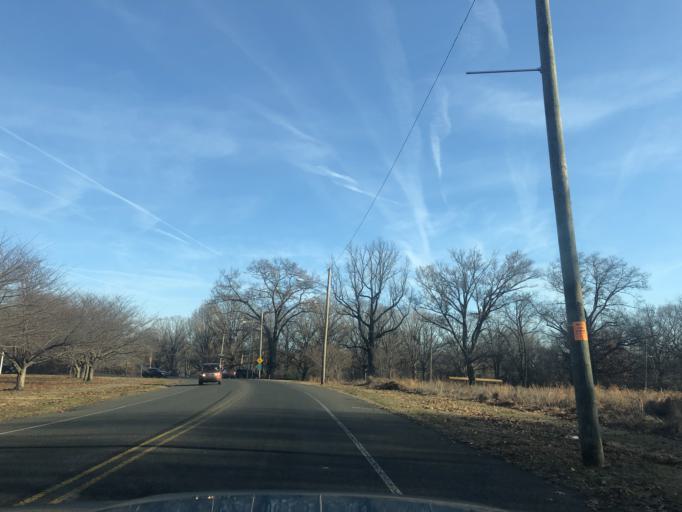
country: US
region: Pennsylvania
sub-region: Montgomery County
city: Bala-Cynwyd
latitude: 39.9891
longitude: -75.2200
